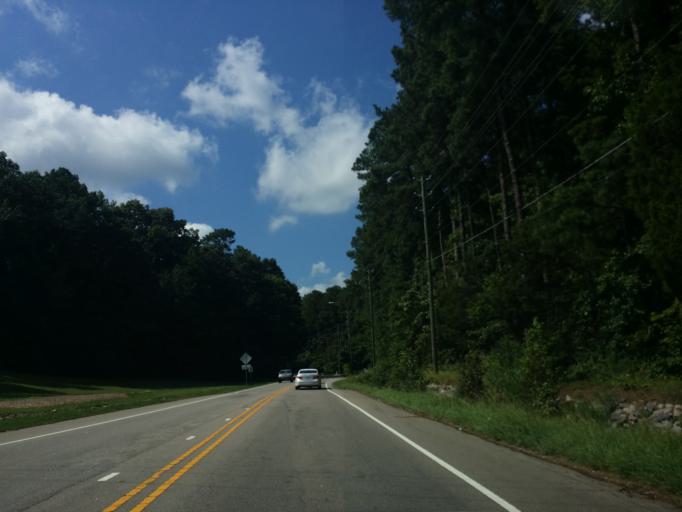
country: US
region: North Carolina
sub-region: Wake County
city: West Raleigh
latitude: 35.8738
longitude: -78.7012
